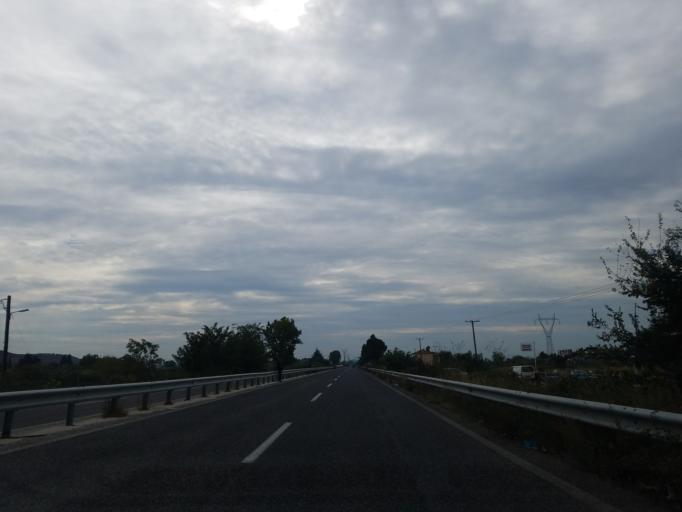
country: GR
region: Thessaly
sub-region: Trikala
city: Vasiliki
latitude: 39.6388
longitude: 21.6955
